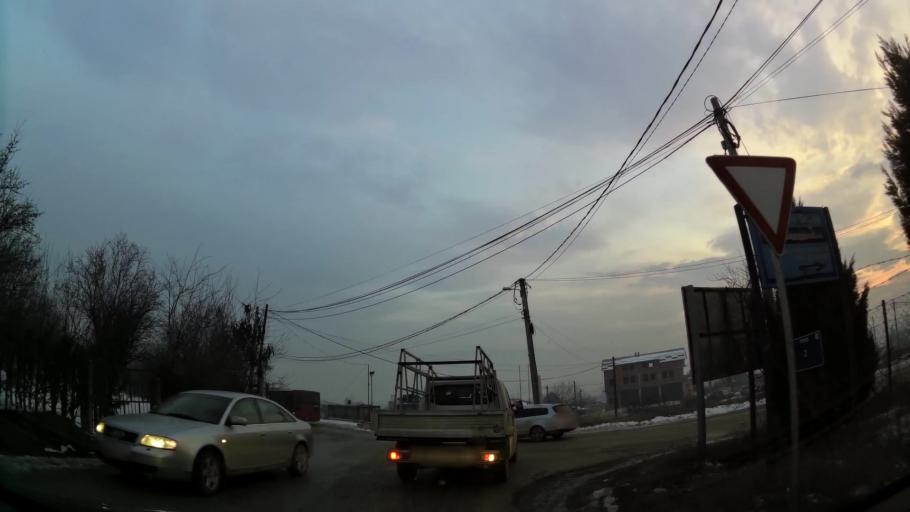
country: MK
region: Suto Orizari
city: Suto Orizare
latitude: 42.0301
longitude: 21.4069
